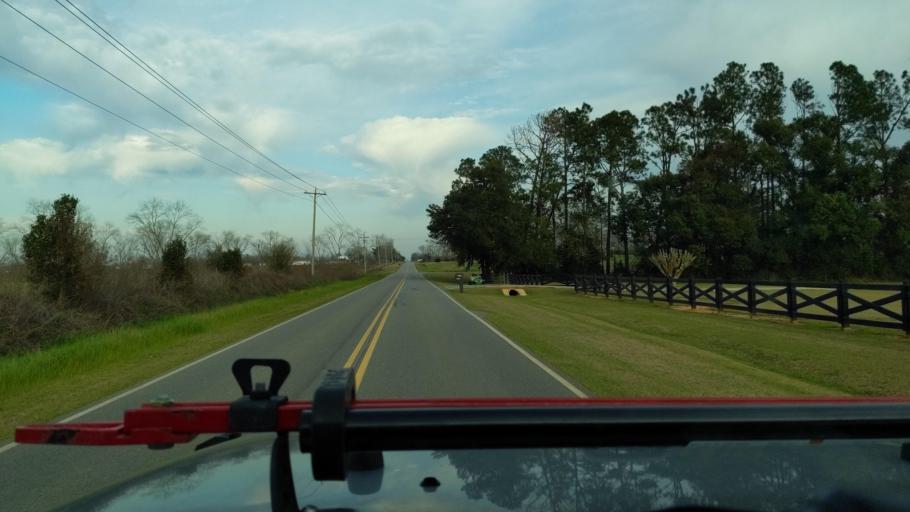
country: US
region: Alabama
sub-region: Baldwin County
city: Foley
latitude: 30.4580
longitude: -87.7273
